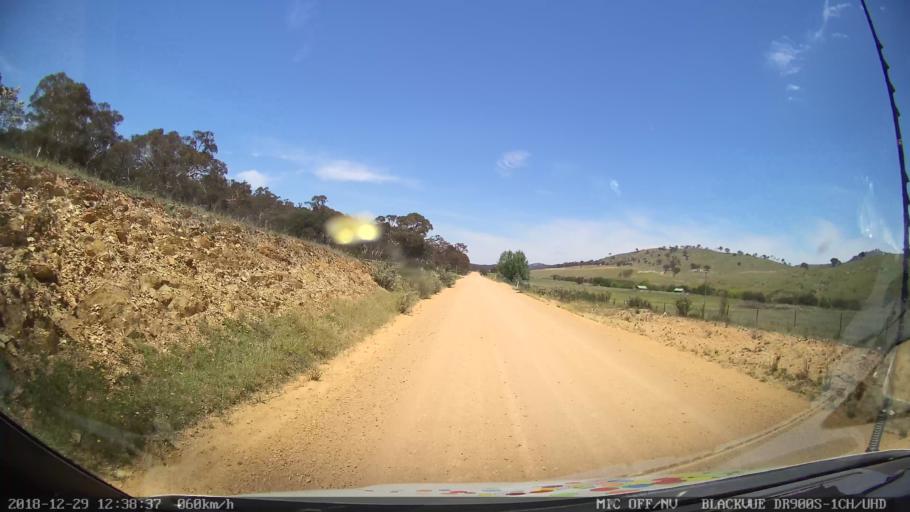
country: AU
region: Australian Capital Territory
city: Macarthur
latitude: -35.5904
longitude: 149.2288
